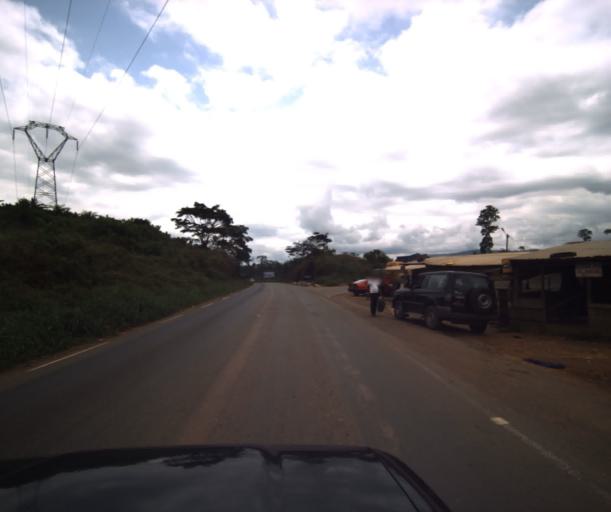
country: CM
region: Centre
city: Eseka
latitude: 3.8844
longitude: 10.8458
